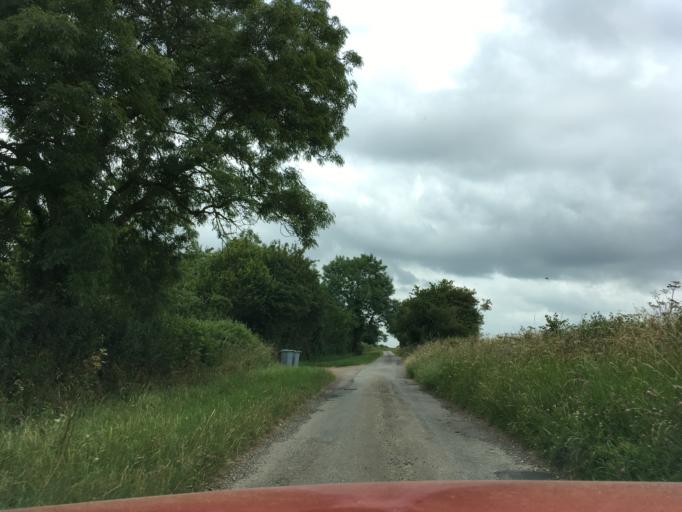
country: GB
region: England
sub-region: Oxfordshire
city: Chipping Norton
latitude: 51.9151
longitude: -1.5055
